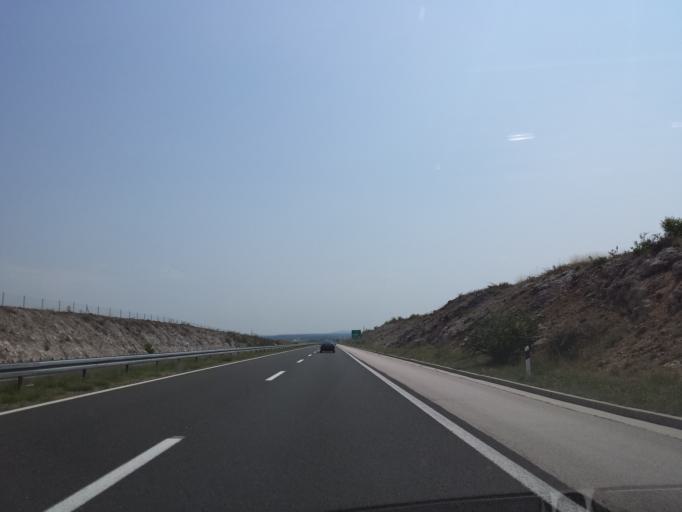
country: HR
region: Zadarska
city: Polaca
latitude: 44.0728
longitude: 15.5173
